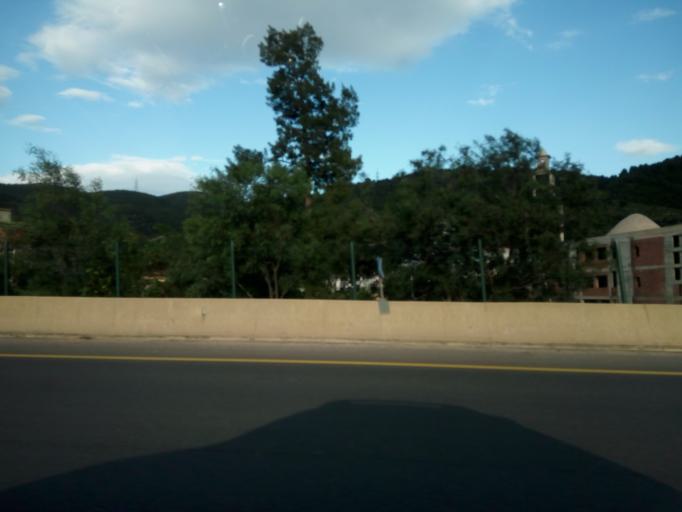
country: DZ
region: Tipaza
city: El Affroun
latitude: 36.4213
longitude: 2.5667
